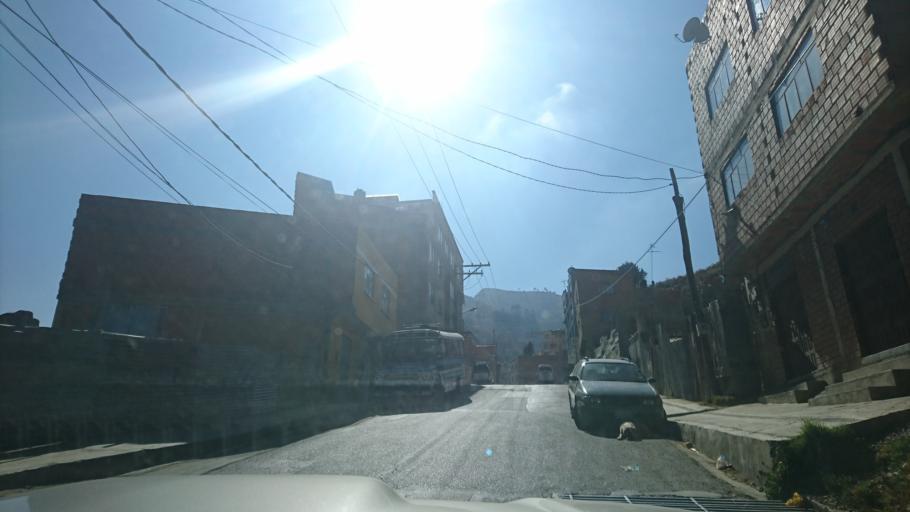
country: BO
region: La Paz
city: La Paz
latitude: -16.4813
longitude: -68.1157
